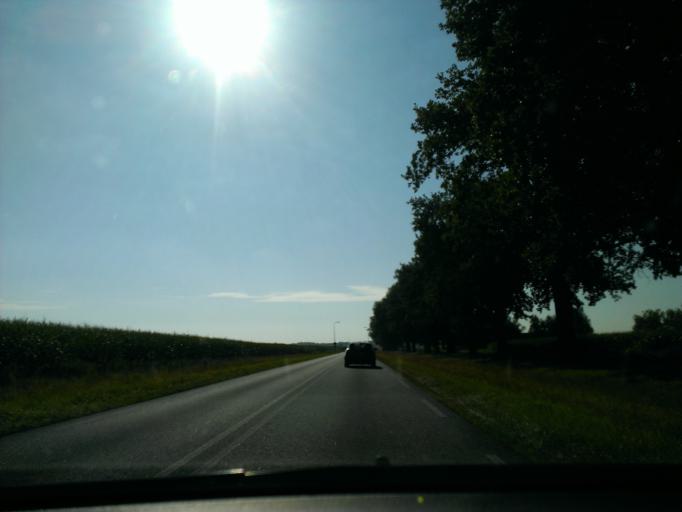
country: NL
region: Drenthe
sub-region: Gemeente Coevorden
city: Dalen
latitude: 52.7218
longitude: 6.7353
